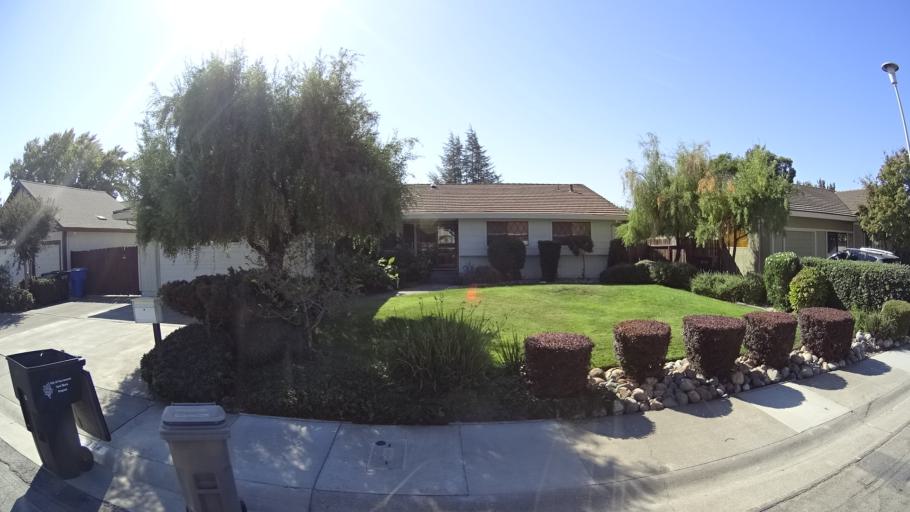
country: US
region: California
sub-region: Sacramento County
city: Parkway
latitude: 38.4966
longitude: -121.5328
